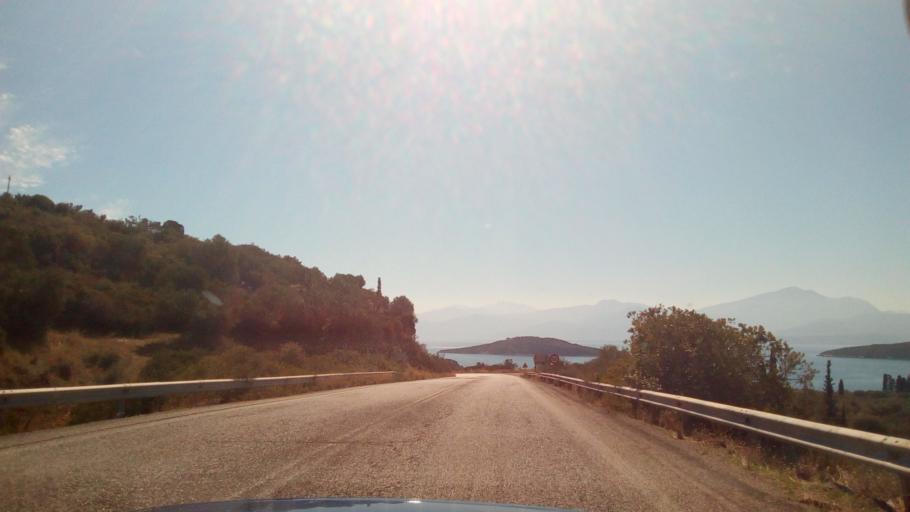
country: GR
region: West Greece
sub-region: Nomos Achaias
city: Selianitika
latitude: 38.3794
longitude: 22.0938
